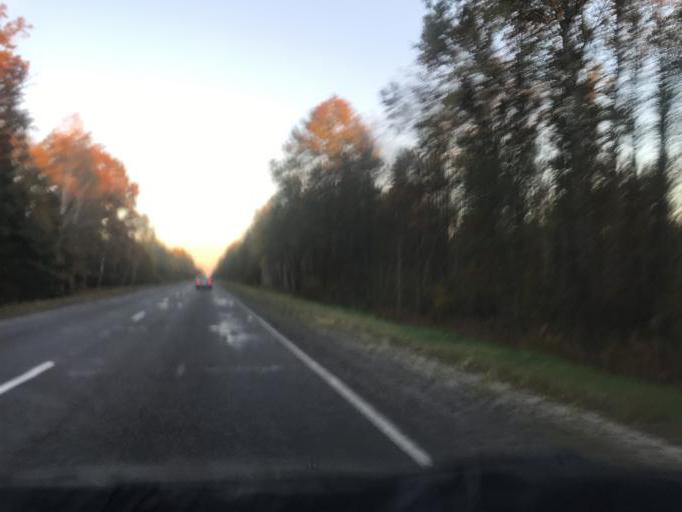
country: BY
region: Gomel
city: Mazyr
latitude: 52.1910
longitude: 29.1242
